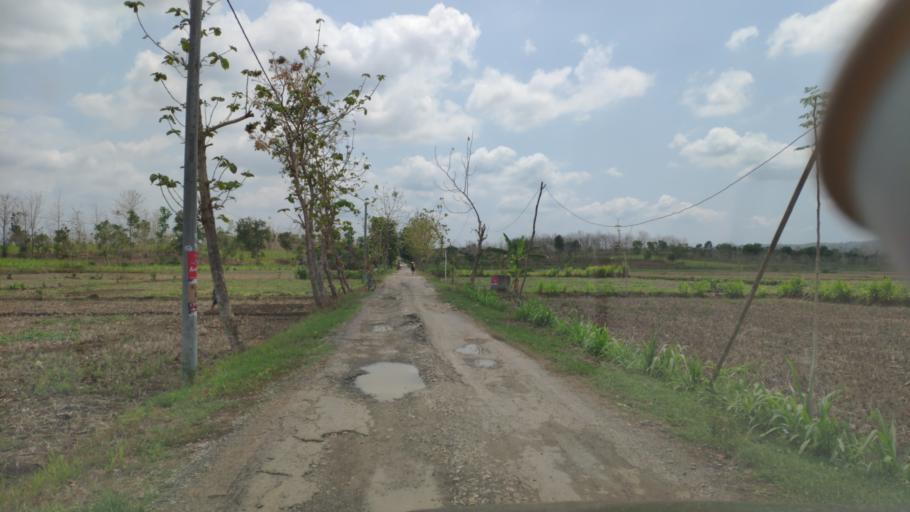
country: ID
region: Central Java
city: Klopoduwur
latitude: -7.0286
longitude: 111.3970
